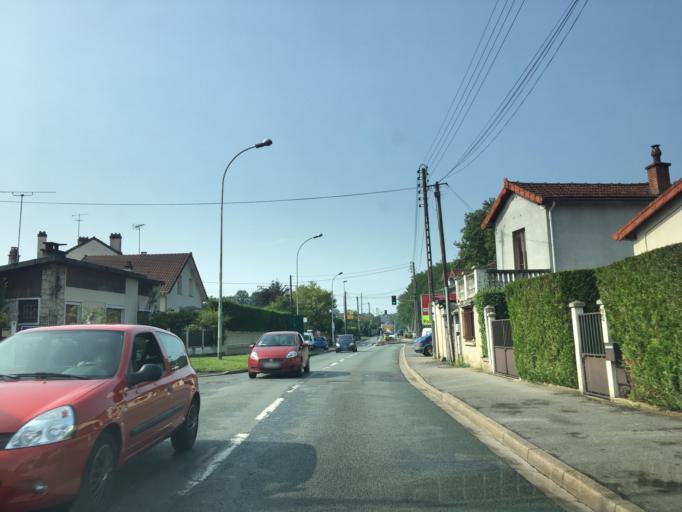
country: FR
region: Ile-de-France
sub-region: Departement du Val-de-Marne
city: Sucy-en-Brie
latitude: 48.7567
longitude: 2.5275
